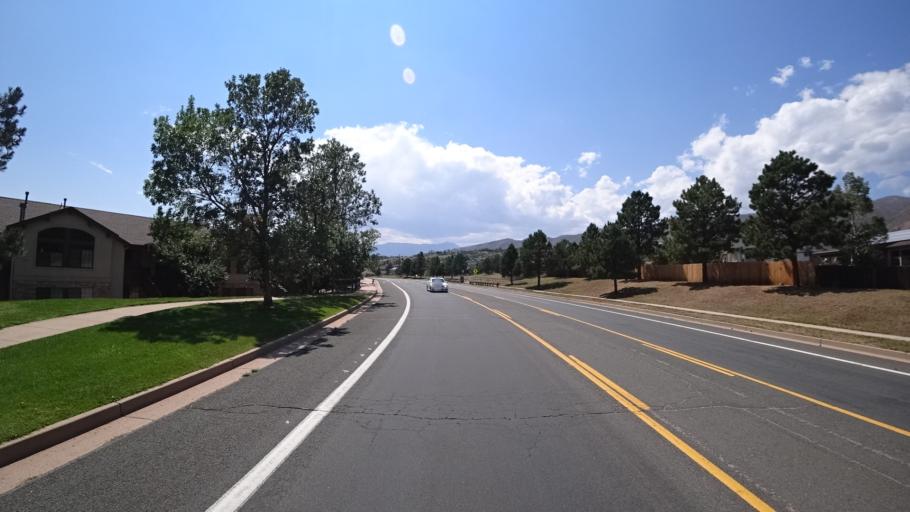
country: US
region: Colorado
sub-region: El Paso County
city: Air Force Academy
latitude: 38.9275
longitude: -104.8662
